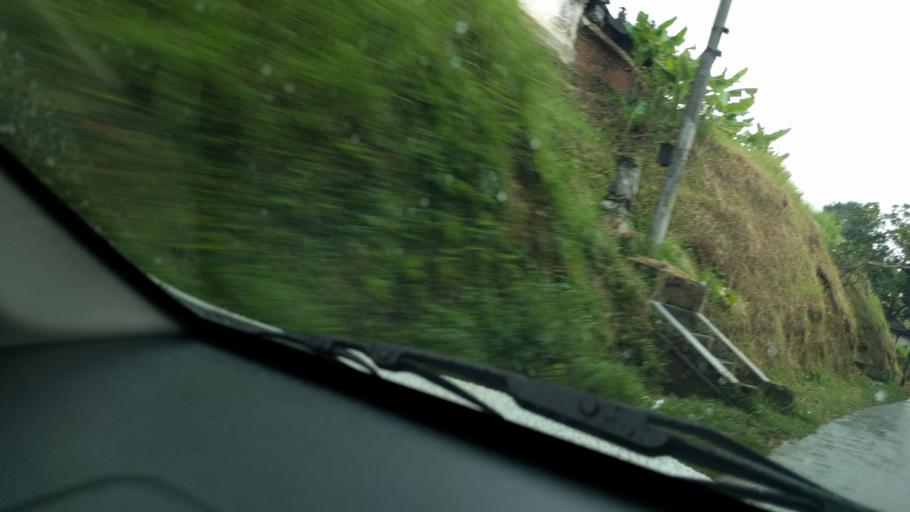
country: ID
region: Bali
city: Bunutan
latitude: -8.4762
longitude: 115.2591
